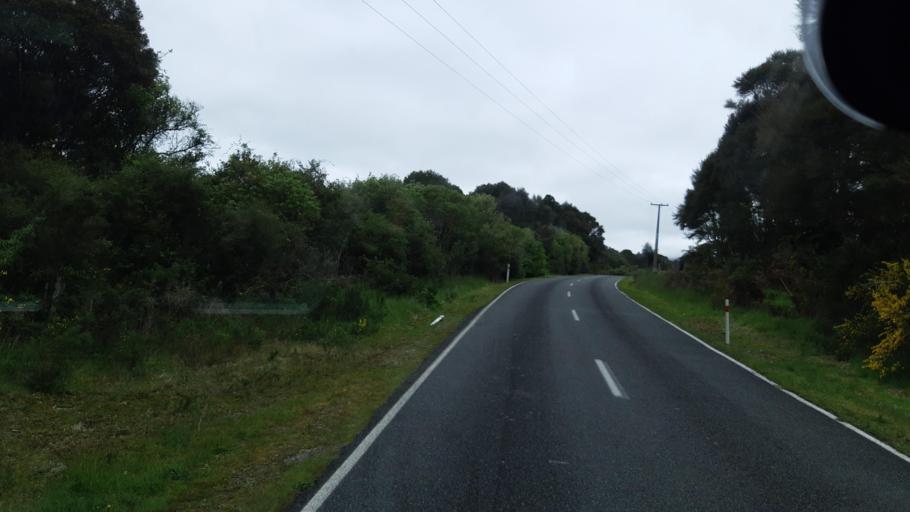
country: NZ
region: West Coast
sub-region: Grey District
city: Greymouth
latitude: -42.6355
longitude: 171.2789
